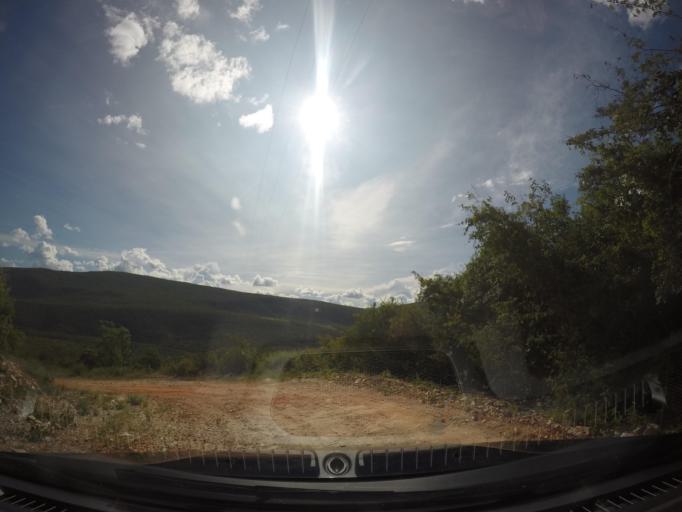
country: BR
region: Bahia
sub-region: Barra Da Estiva
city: Barra da Estiva
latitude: -13.2180
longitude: -41.5964
